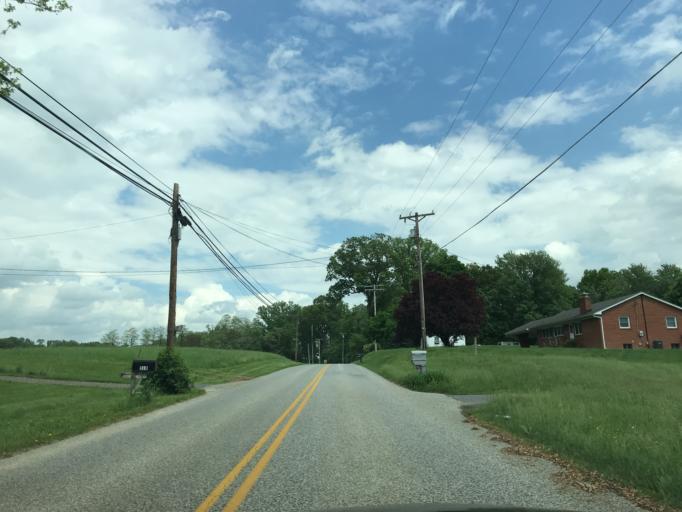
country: US
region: Maryland
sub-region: Harford County
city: Bel Air North
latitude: 39.6106
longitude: -76.3637
